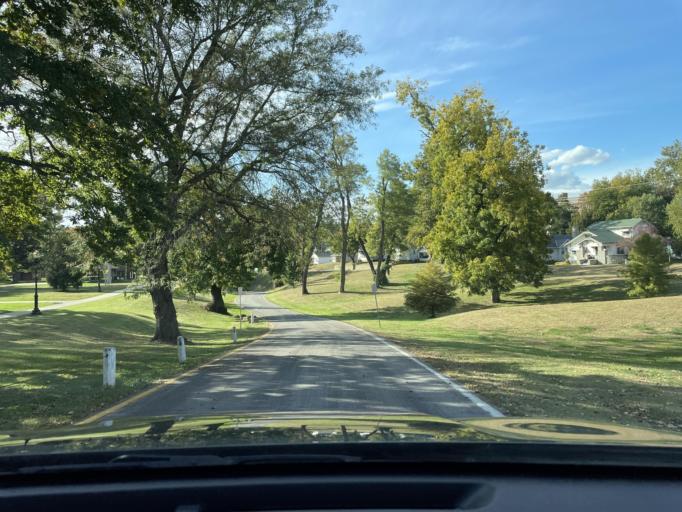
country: US
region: Kansas
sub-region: Doniphan County
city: Elwood
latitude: 39.7111
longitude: -94.8511
